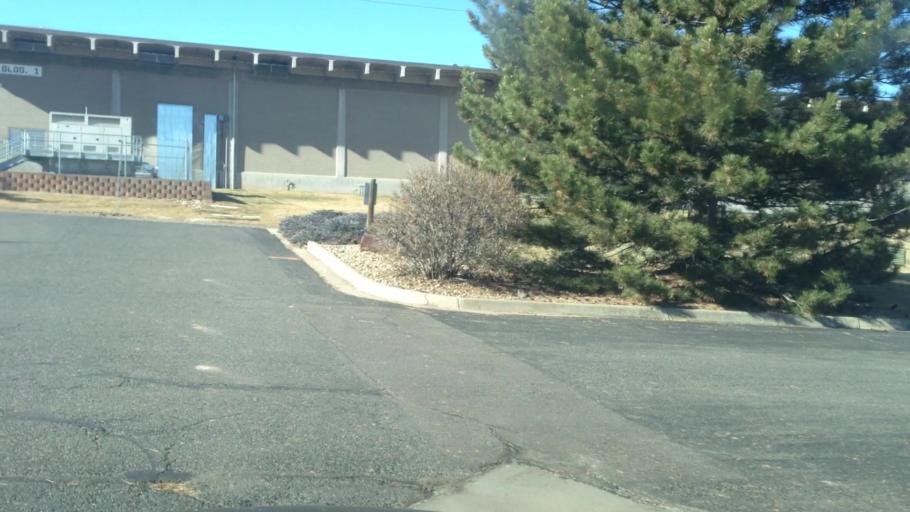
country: US
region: Colorado
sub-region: Jefferson County
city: Applewood
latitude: 39.7296
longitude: -105.1234
